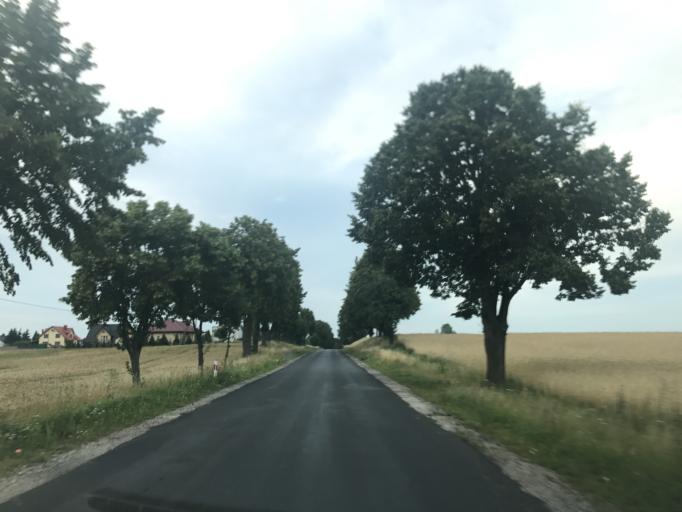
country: PL
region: Kujawsko-Pomorskie
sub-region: Powiat lipnowski
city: Lipno
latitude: 52.8272
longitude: 19.1840
